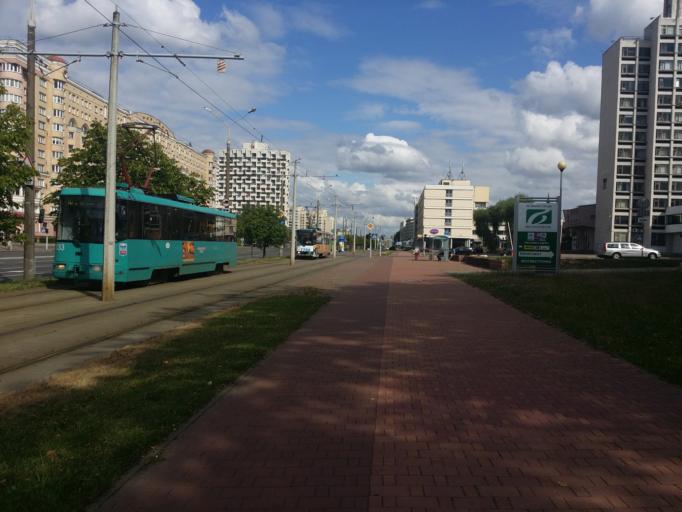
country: BY
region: Minsk
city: Minsk
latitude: 53.9175
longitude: 27.5552
